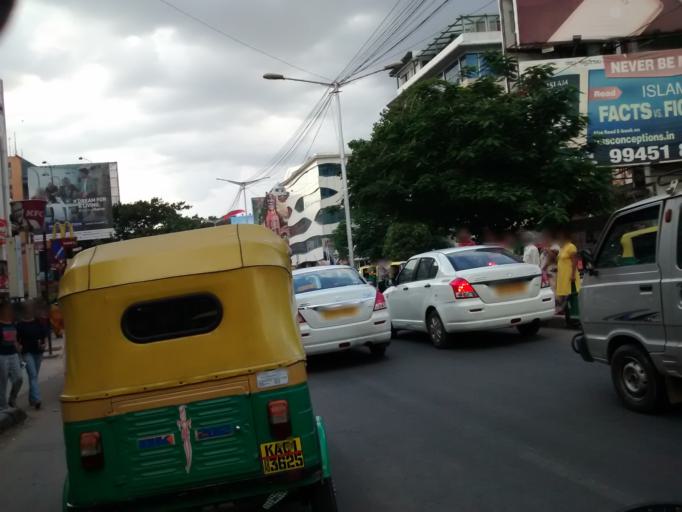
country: IN
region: Karnataka
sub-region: Bangalore Urban
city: Bangalore
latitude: 12.9592
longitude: 77.6574
